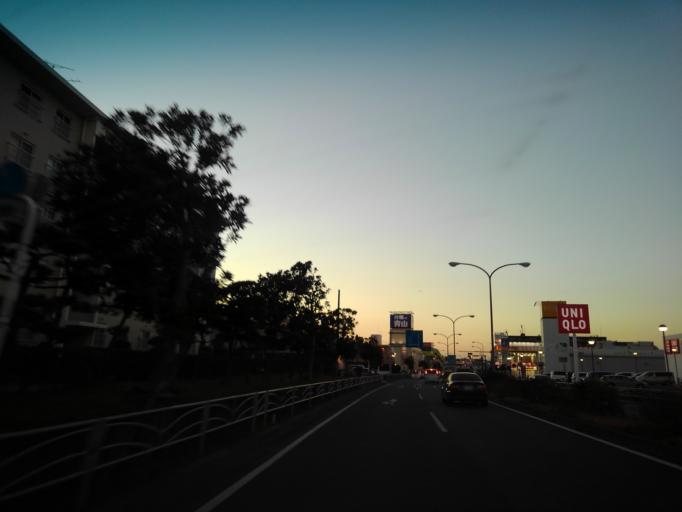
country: JP
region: Kanagawa
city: Yokosuka
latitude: 35.2640
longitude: 139.6955
